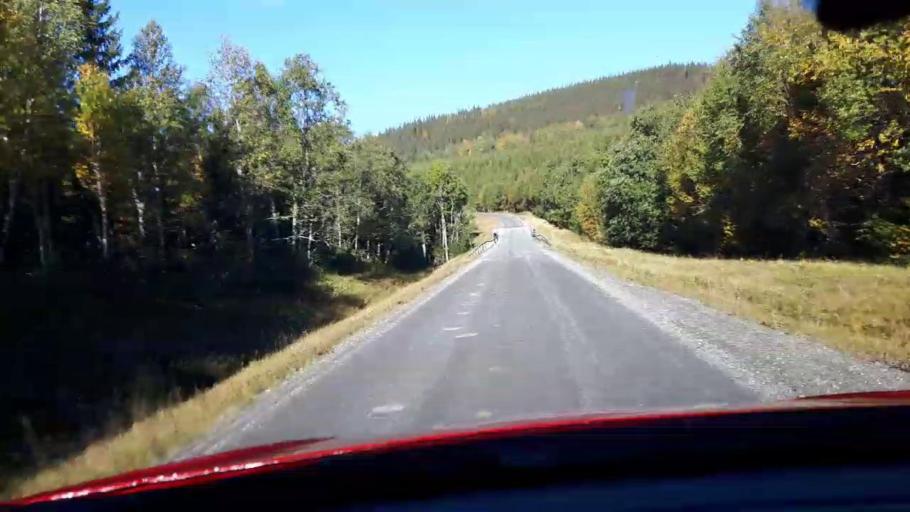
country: NO
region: Nord-Trondelag
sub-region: Lierne
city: Sandvika
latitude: 64.5893
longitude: 13.8588
